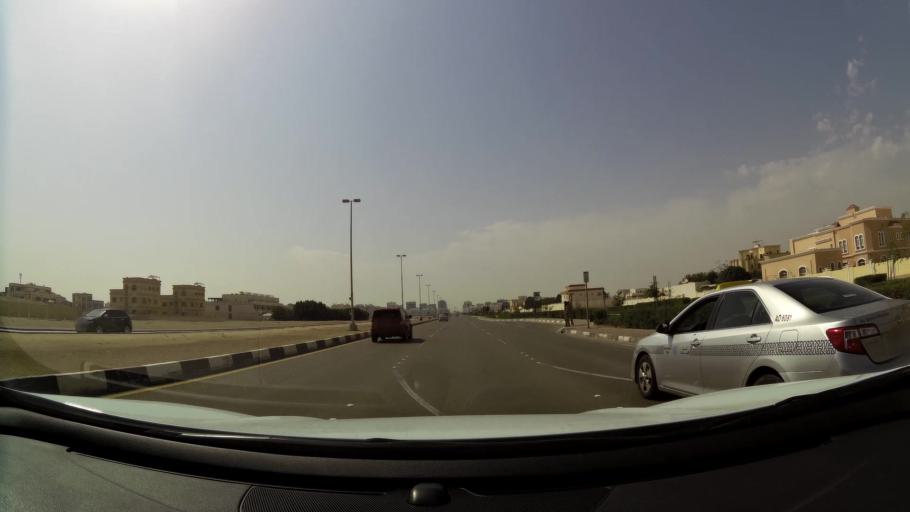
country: AE
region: Abu Dhabi
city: Abu Dhabi
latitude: 24.3252
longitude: 54.5493
